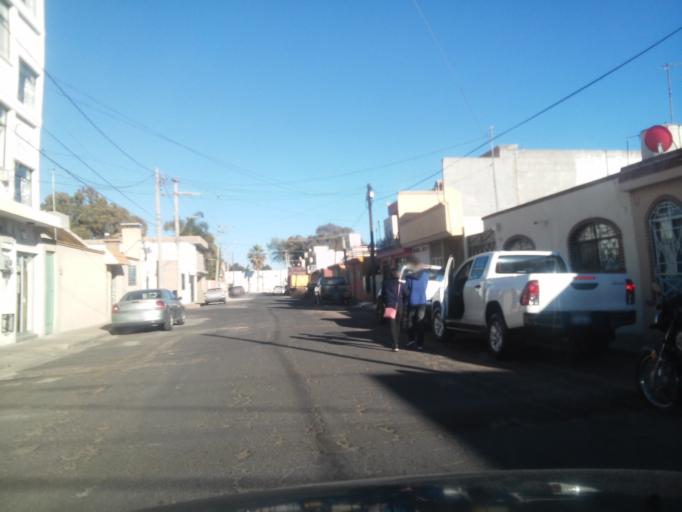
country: MX
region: Durango
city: Victoria de Durango
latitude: 24.0318
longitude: -104.6494
